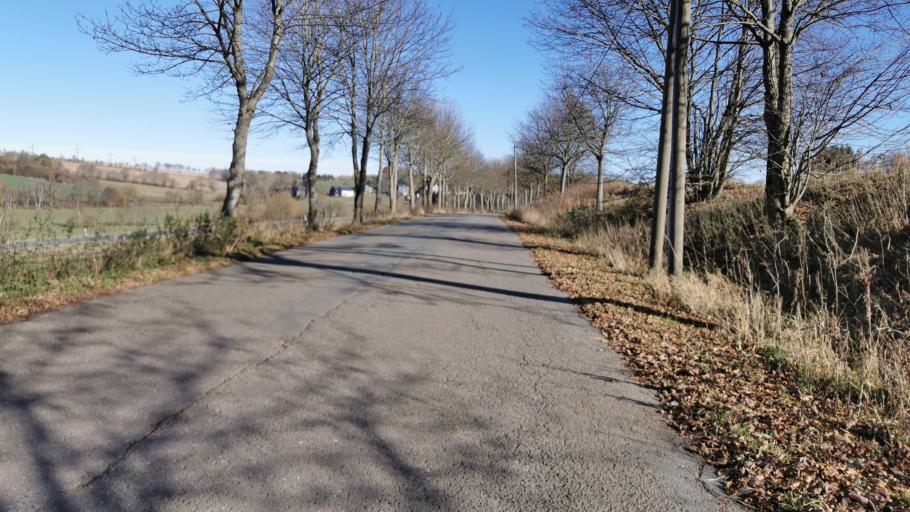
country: DE
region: Bavaria
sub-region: Upper Franconia
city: Ludwigsstadt
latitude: 50.4713
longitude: 11.4366
